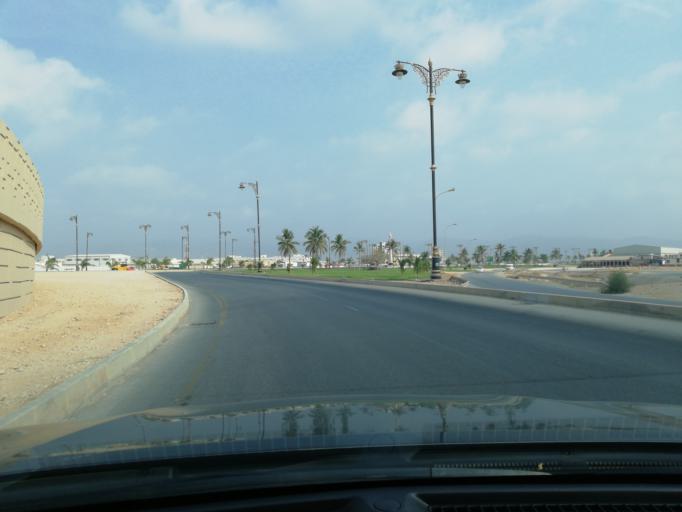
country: OM
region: Zufar
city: Salalah
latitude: 17.0193
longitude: 54.0589
